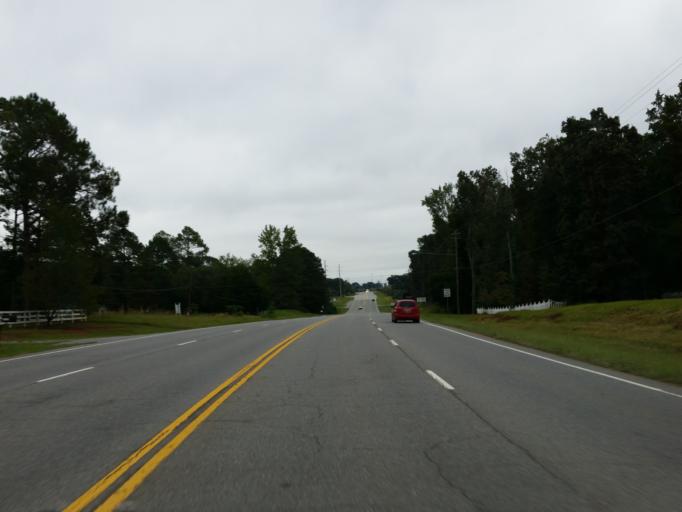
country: US
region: Georgia
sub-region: Houston County
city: Perry
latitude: 32.4791
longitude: -83.7543
